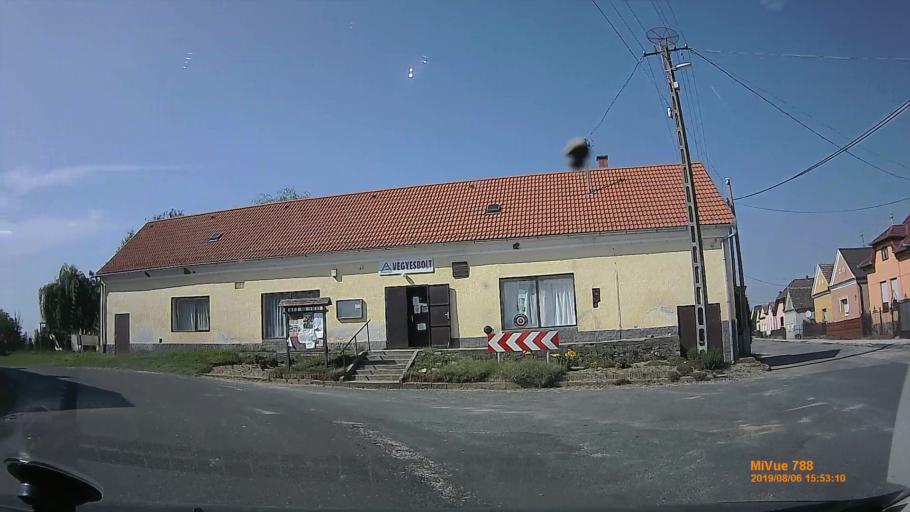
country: HU
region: Somogy
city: Csurgo
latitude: 46.2870
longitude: 17.0341
